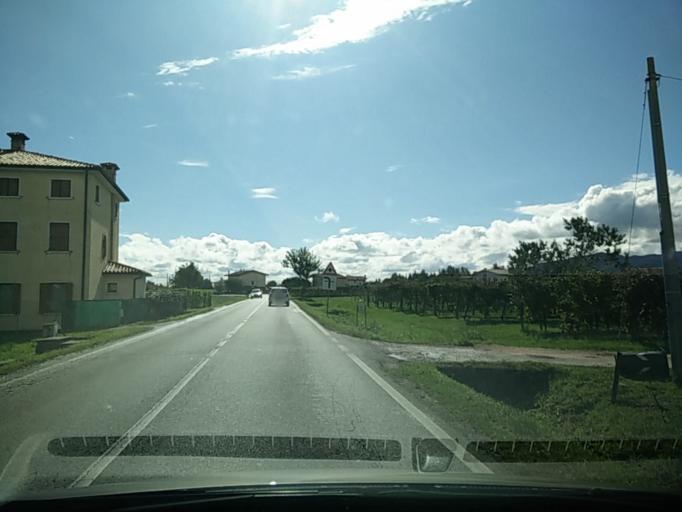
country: IT
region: Veneto
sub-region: Provincia di Treviso
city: Bigolino
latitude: 45.8752
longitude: 12.0037
